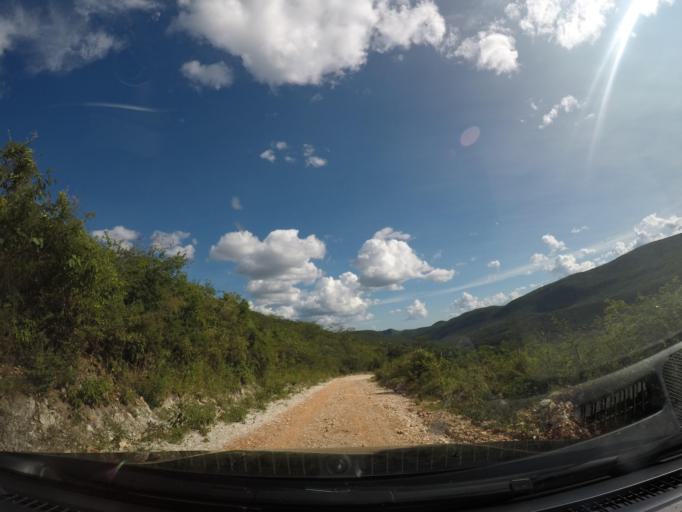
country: BR
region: Bahia
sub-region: Barra Da Estiva
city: Barra da Estiva
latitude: -13.2188
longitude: -41.5965
